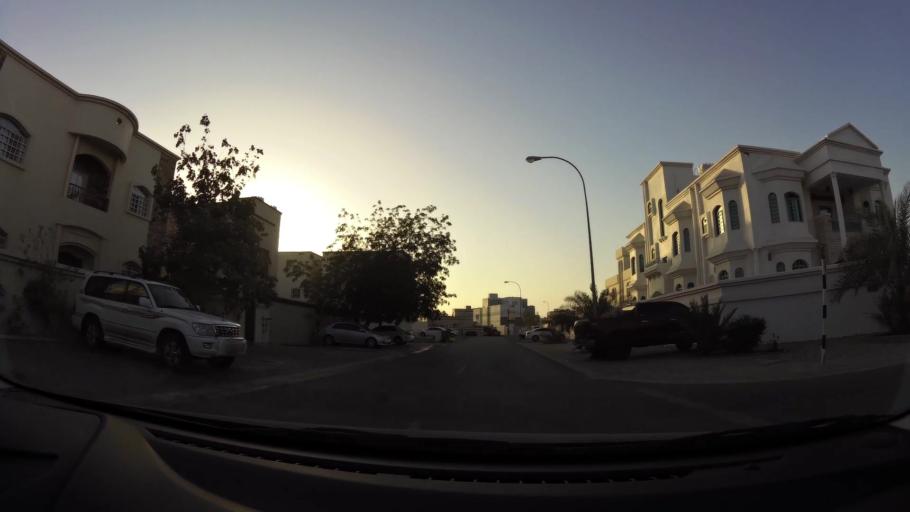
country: OM
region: Muhafazat Masqat
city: As Sib al Jadidah
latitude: 23.6109
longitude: 58.1981
